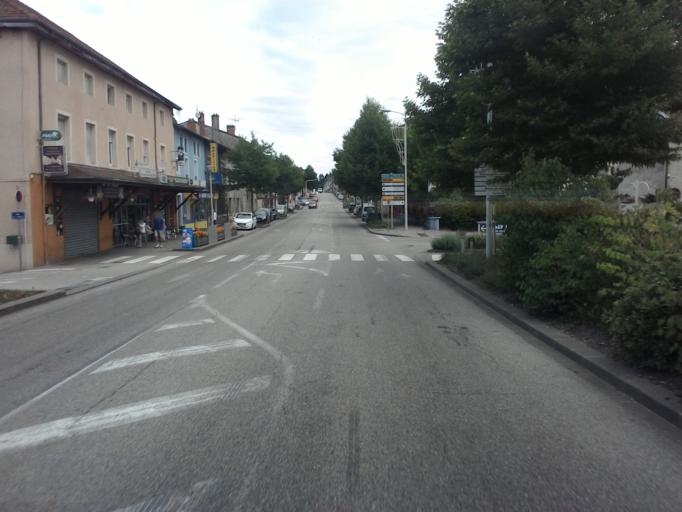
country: FR
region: Rhone-Alpes
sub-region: Departement de l'Ain
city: Ambronay
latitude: 46.0478
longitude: 5.3360
